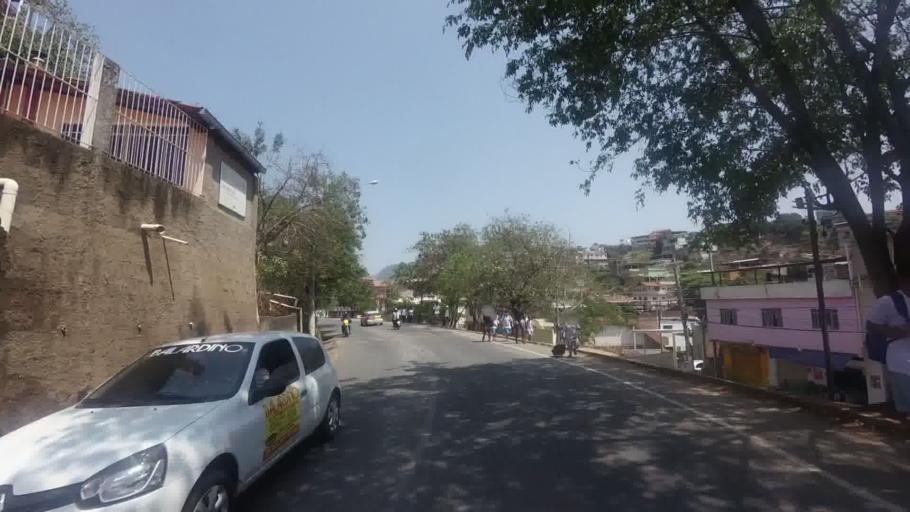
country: BR
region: Espirito Santo
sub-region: Cachoeiro De Itapemirim
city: Cachoeiro de Itapemirim
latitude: -20.8501
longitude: -41.1488
